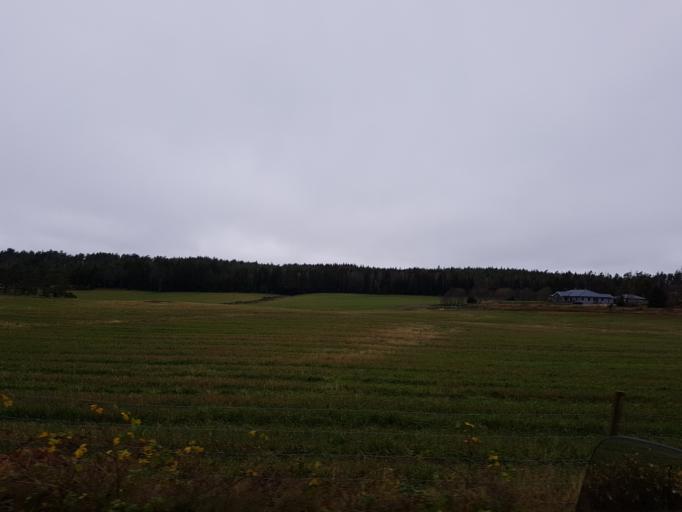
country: SE
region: Vaestra Goetaland
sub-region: Orust
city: Henan
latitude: 58.2173
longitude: 11.7698
